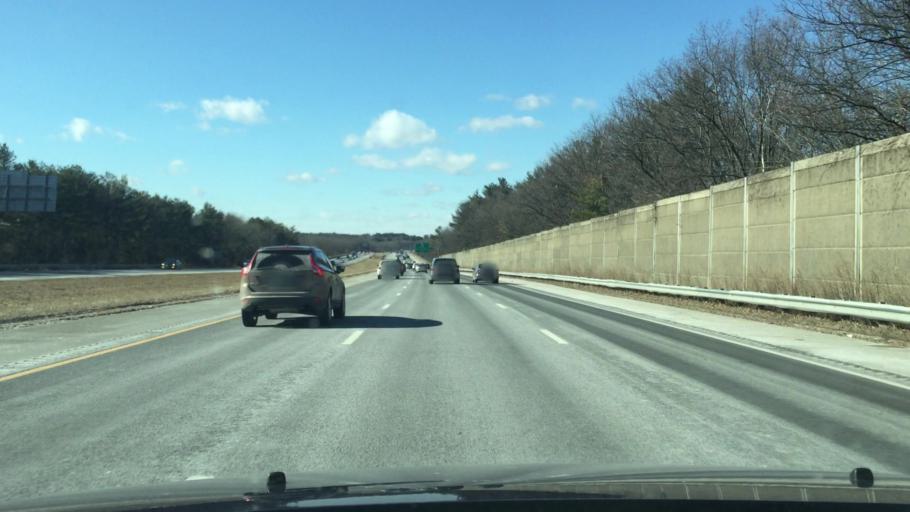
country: US
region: Massachusetts
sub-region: Middlesex County
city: Chelmsford
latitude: 42.6260
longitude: -71.3819
